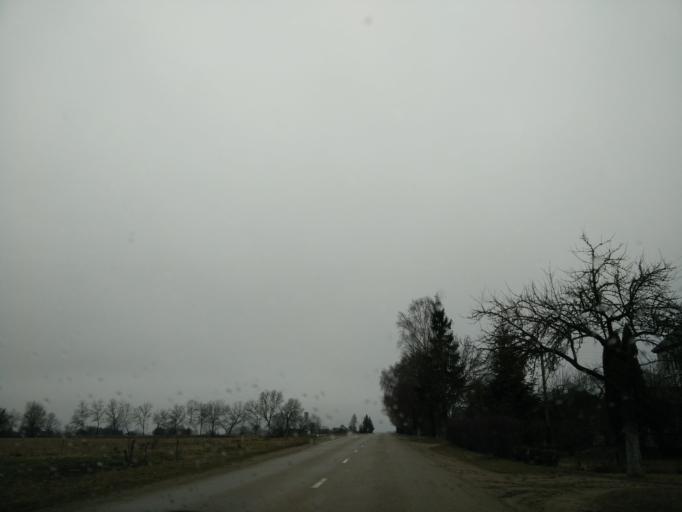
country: LT
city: Ariogala
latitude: 55.3257
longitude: 23.4236
